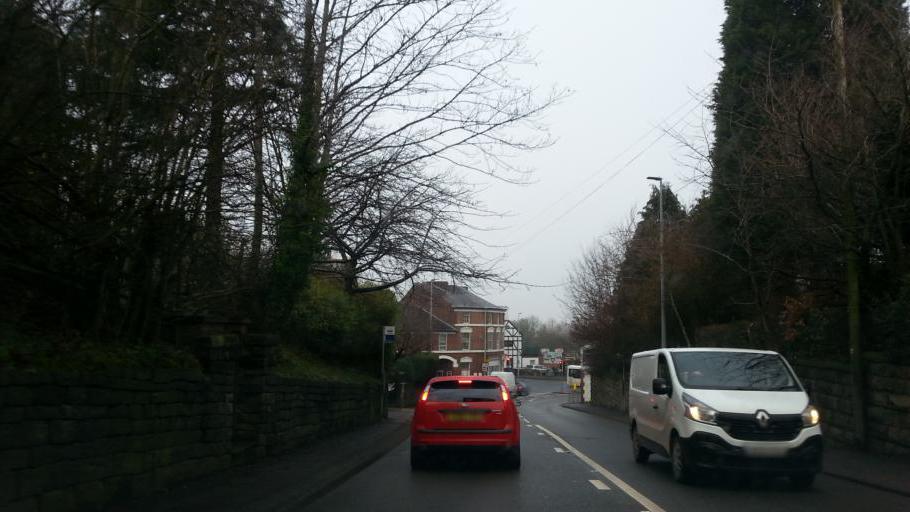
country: GB
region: England
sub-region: Cheshire East
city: Congleton
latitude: 53.1622
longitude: -2.2049
